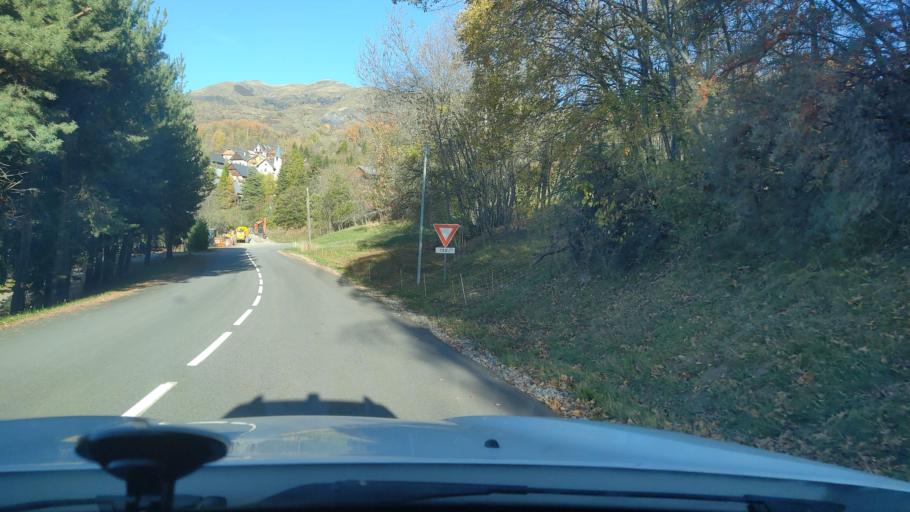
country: FR
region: Rhone-Alpes
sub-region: Departement de la Savoie
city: Saint-Jean-de-Maurienne
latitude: 45.2549
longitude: 6.2940
